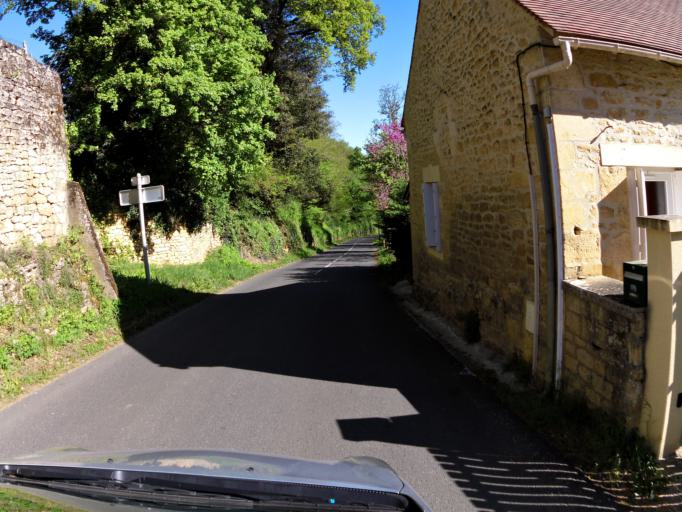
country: FR
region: Aquitaine
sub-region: Departement de la Dordogne
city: Carsac-Aillac
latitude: 44.8329
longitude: 1.3103
